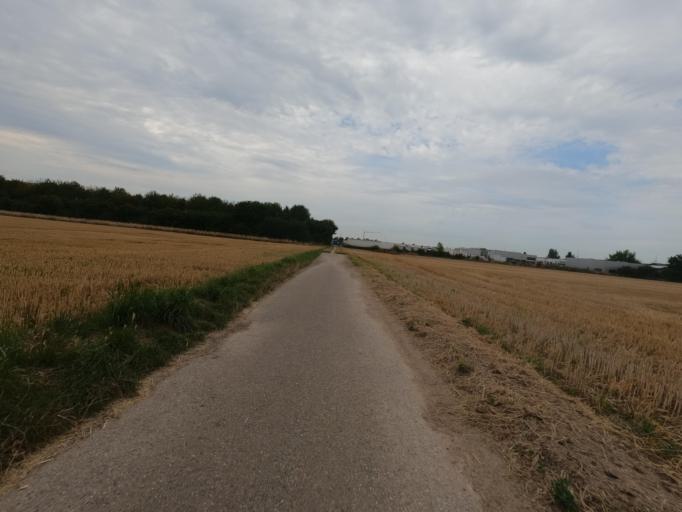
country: DE
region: North Rhine-Westphalia
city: Geilenkirchen
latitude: 50.9734
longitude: 6.1009
